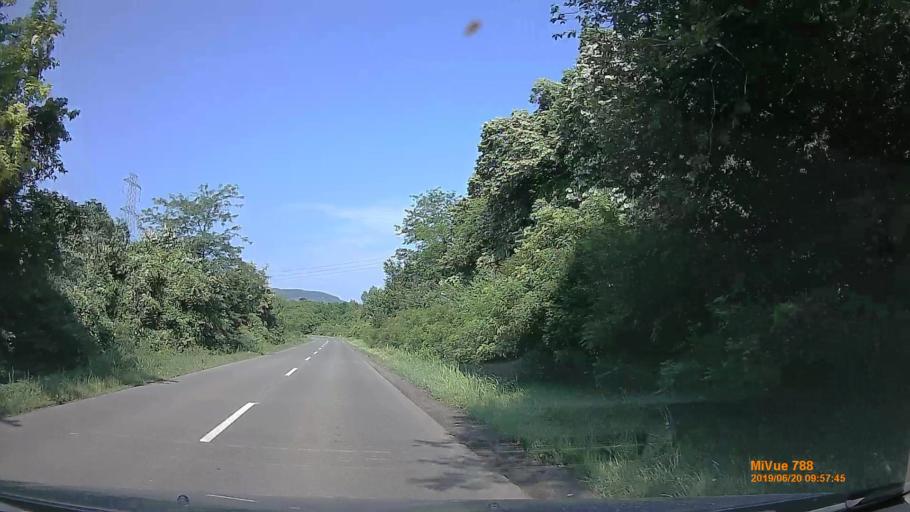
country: HU
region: Baranya
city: Pecsvarad
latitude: 46.1683
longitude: 18.4556
